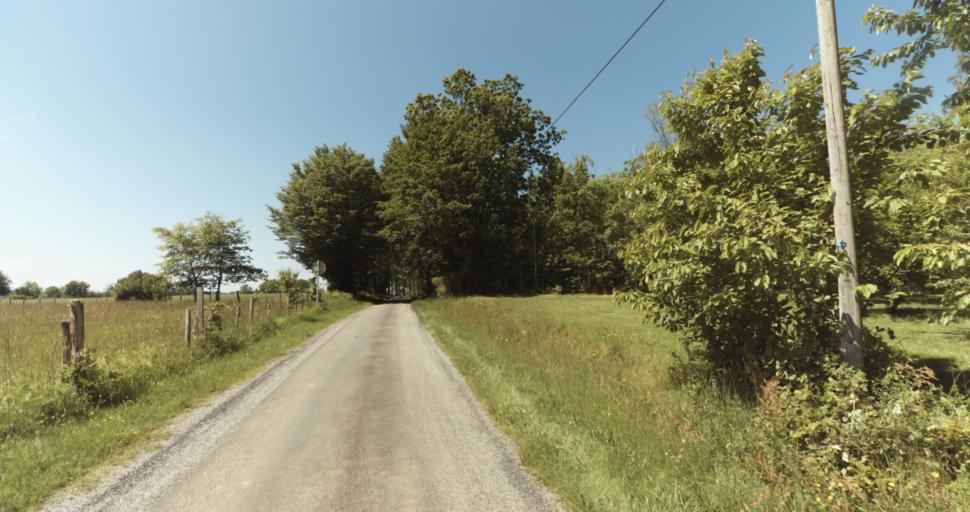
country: FR
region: Limousin
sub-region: Departement de la Haute-Vienne
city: Le Vigen
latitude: 45.7603
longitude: 1.3089
